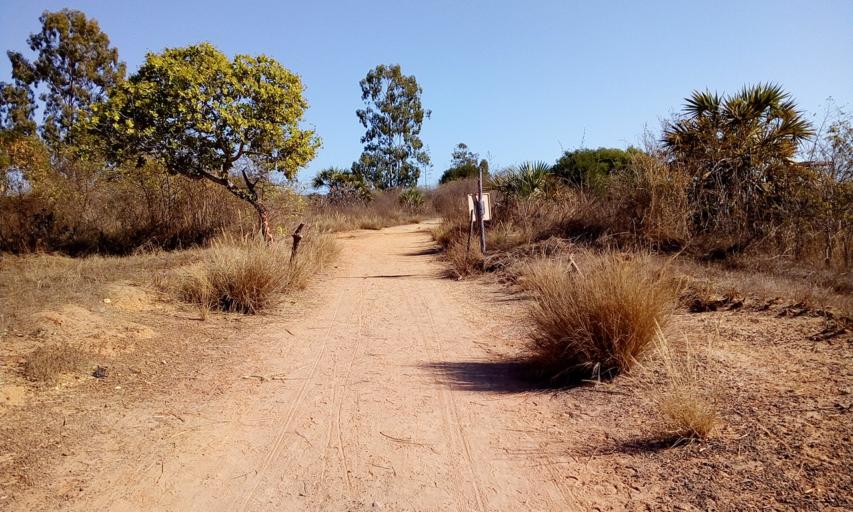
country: MG
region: Boeny
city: Mahajanga
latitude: -15.6263
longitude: 46.4197
